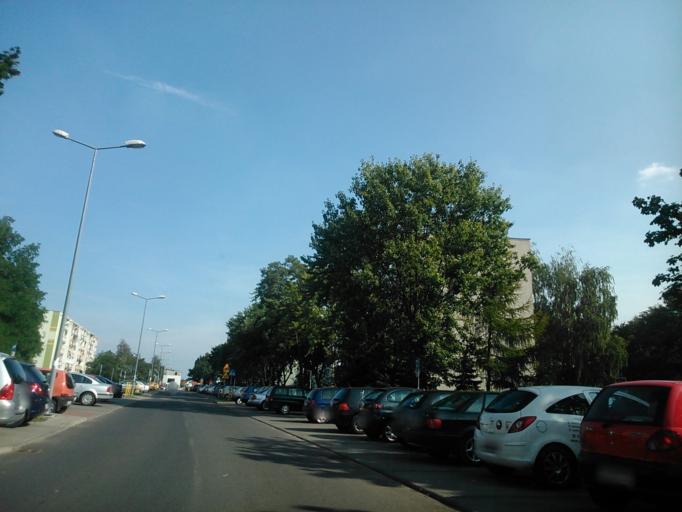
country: PL
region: Kujawsko-Pomorskie
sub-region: Powiat golubsko-dobrzynski
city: Golub-Dobrzyn
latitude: 53.1044
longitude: 19.0507
